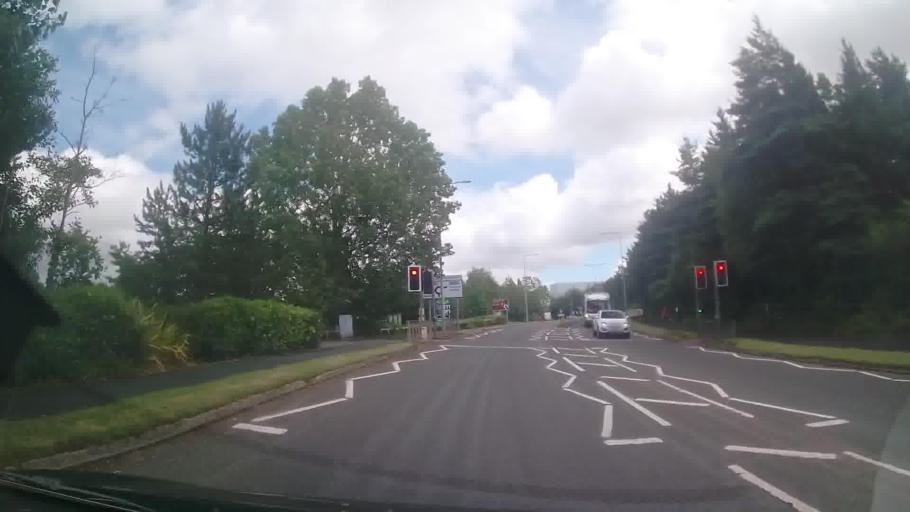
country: GB
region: England
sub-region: Telford and Wrekin
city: Oakengates
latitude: 52.7075
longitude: -2.4337
